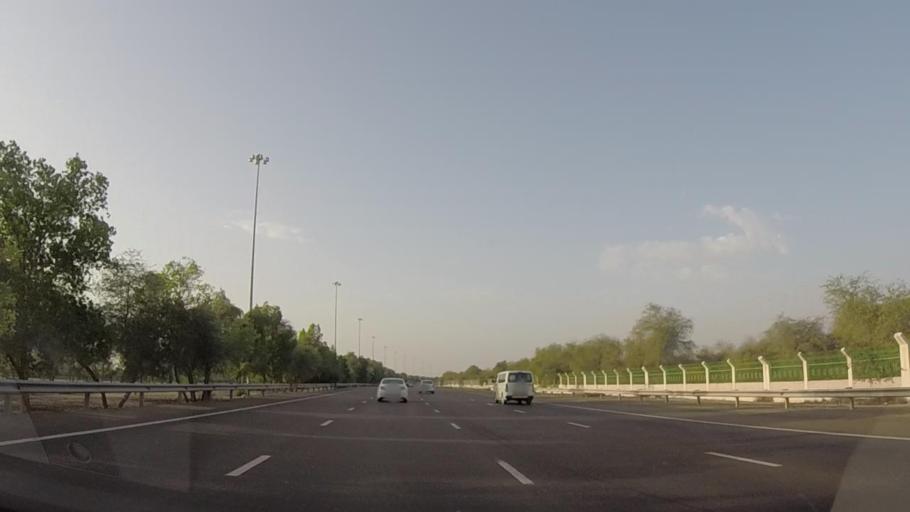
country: AE
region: Dubai
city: Dubai
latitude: 24.7733
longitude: 54.8505
